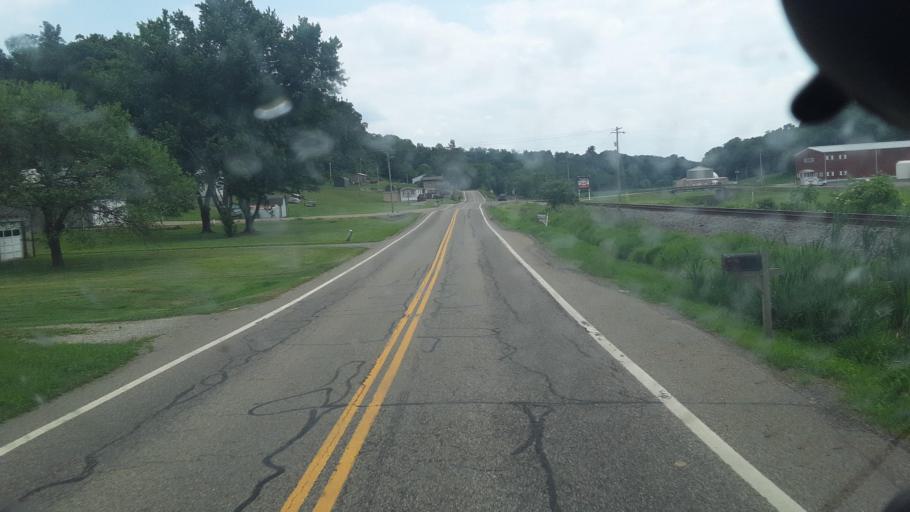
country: US
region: Ohio
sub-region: Coshocton County
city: West Lafayette
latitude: 40.3706
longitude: -81.7271
